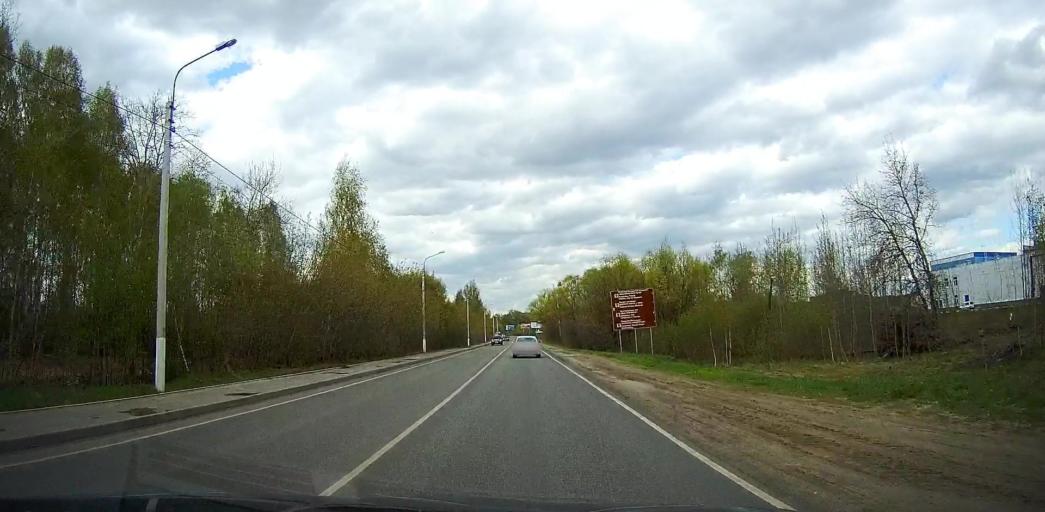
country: RU
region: Moskovskaya
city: Pavlovskiy Posad
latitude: 55.7602
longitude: 38.6563
